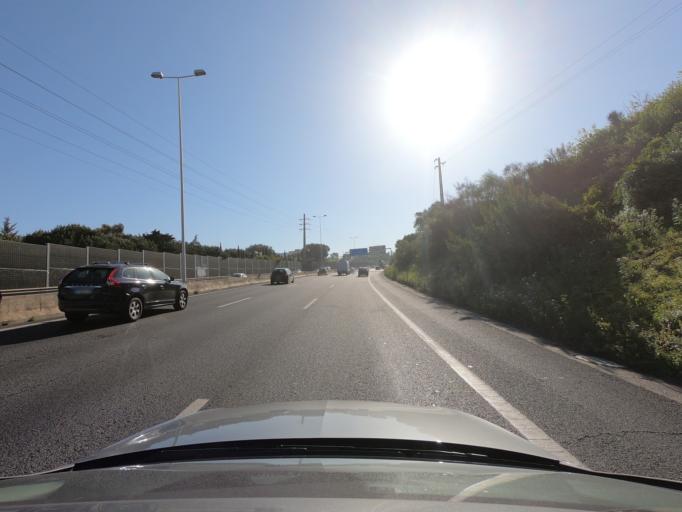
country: PT
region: Lisbon
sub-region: Oeiras
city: Linda-a-Velha
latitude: 38.7207
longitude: -9.2447
